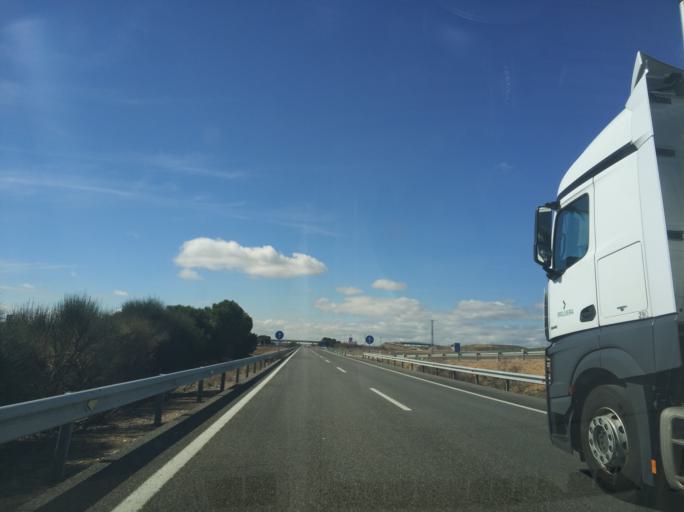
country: ES
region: Castille and Leon
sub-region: Provincia de Burgos
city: Villazopeque
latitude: 42.2018
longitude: -4.0199
